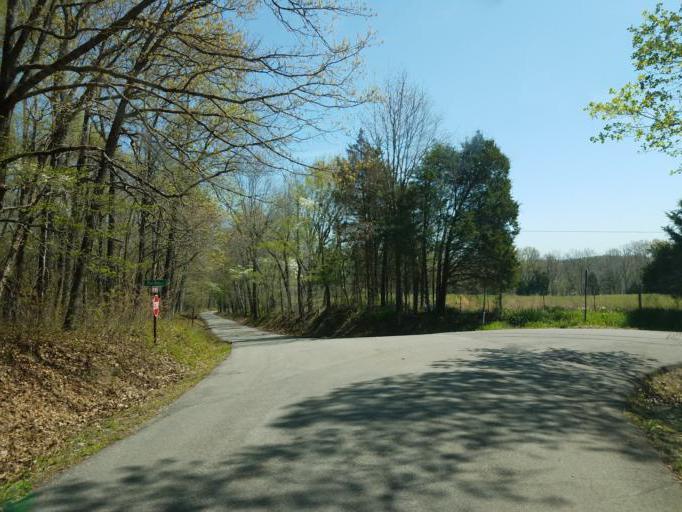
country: US
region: Kentucky
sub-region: Barren County
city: Cave City
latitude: 37.1960
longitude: -86.0458
